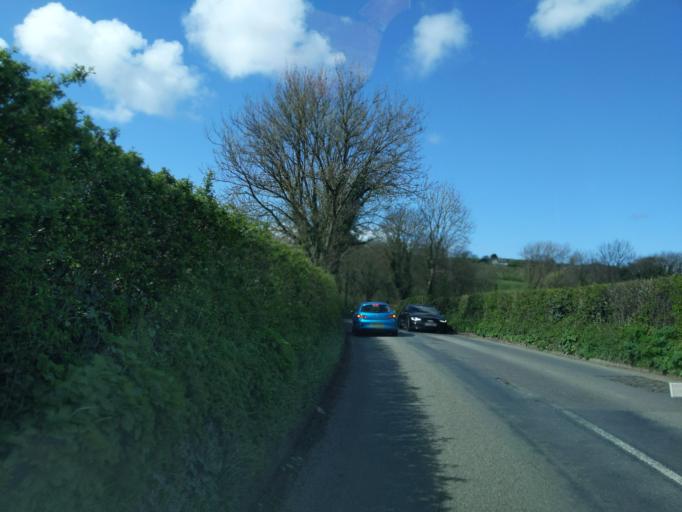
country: GB
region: England
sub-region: Cornwall
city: Wadebridge
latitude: 50.5411
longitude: -4.8560
